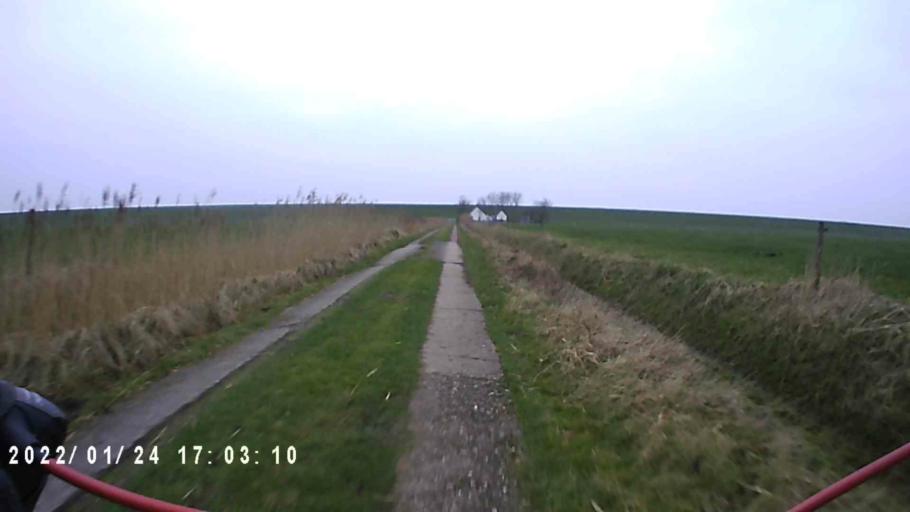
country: NL
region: Groningen
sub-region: Gemeente De Marne
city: Ulrum
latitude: 53.3933
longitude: 6.3202
